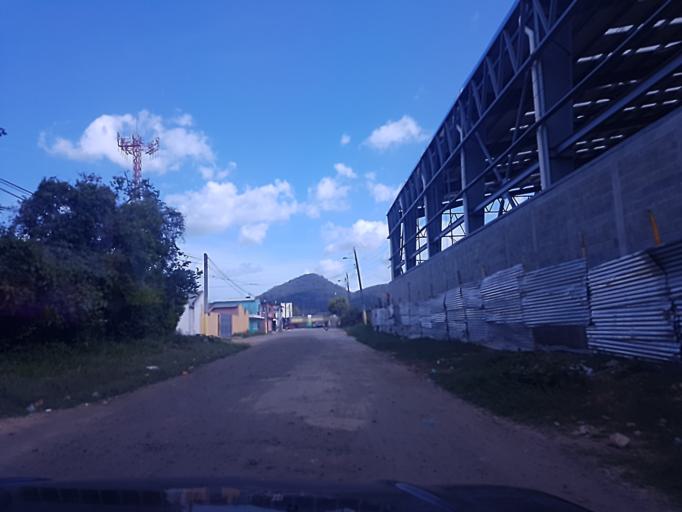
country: GT
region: Guatemala
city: Petapa
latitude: 14.5037
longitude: -90.5567
